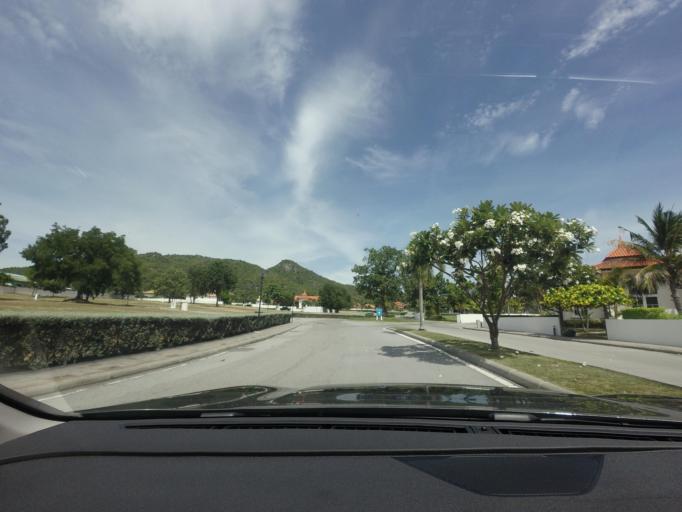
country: TH
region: Prachuap Khiri Khan
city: Hua Hin
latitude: 12.5152
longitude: 99.9623
